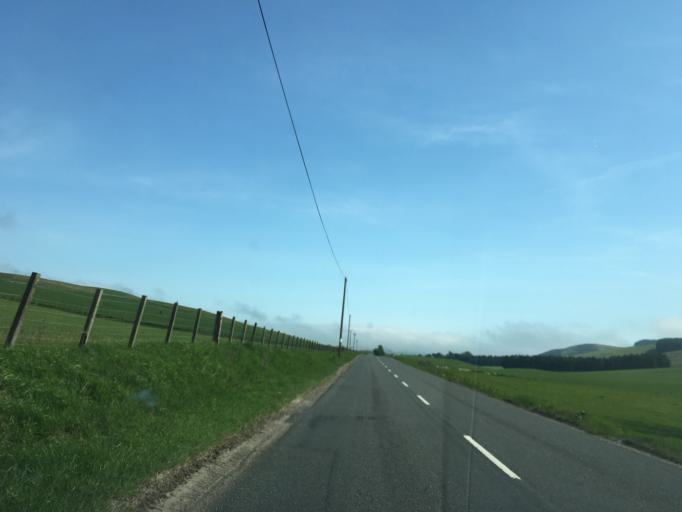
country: GB
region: Scotland
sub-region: South Lanarkshire
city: Biggar
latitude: 55.6657
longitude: -3.4244
